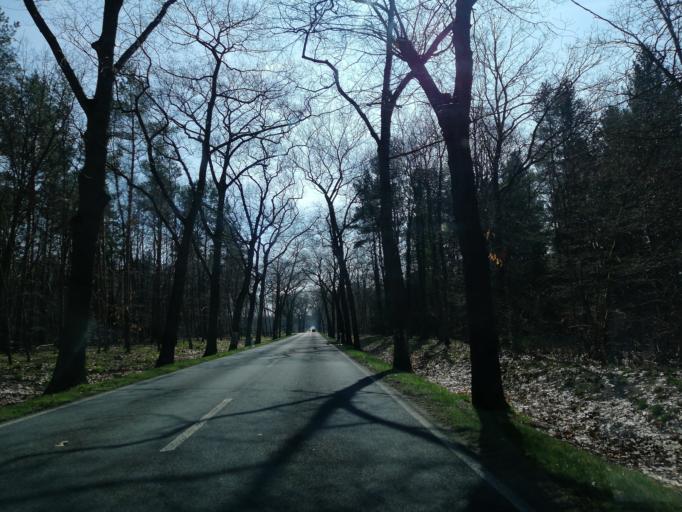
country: DE
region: Brandenburg
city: Altdobern
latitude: 51.6560
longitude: 14.0402
